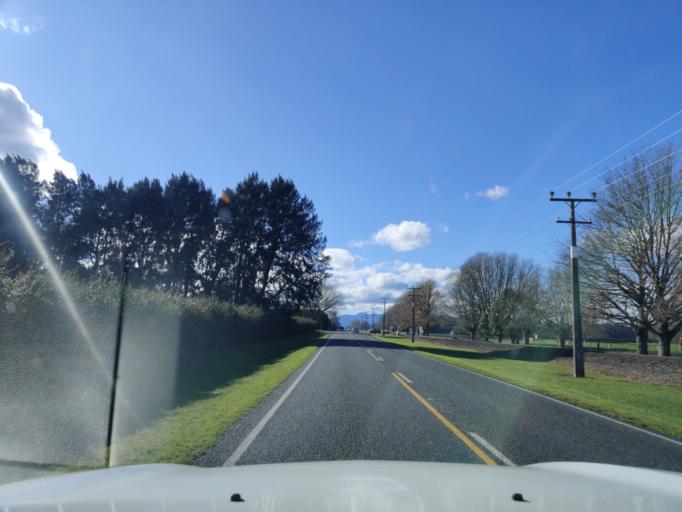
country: NZ
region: Waikato
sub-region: Matamata-Piako District
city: Matamata
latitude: -37.8543
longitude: 175.7576
